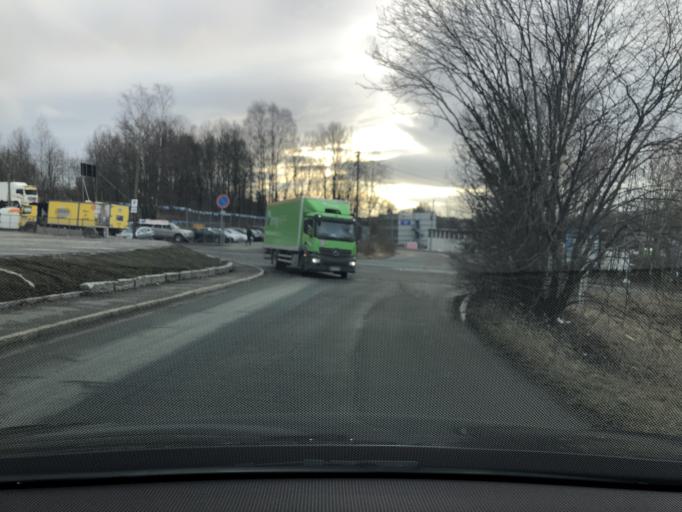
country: NO
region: Oslo
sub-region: Oslo
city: Oslo
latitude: 59.9299
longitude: 10.8457
